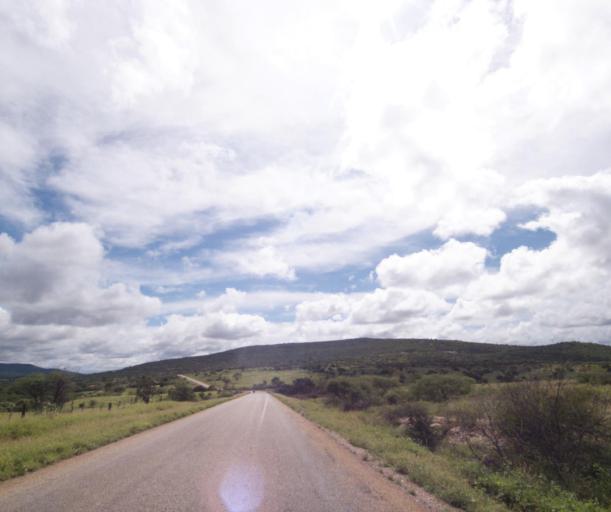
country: BR
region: Bahia
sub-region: Brumado
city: Brumado
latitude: -14.2119
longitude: -41.6334
